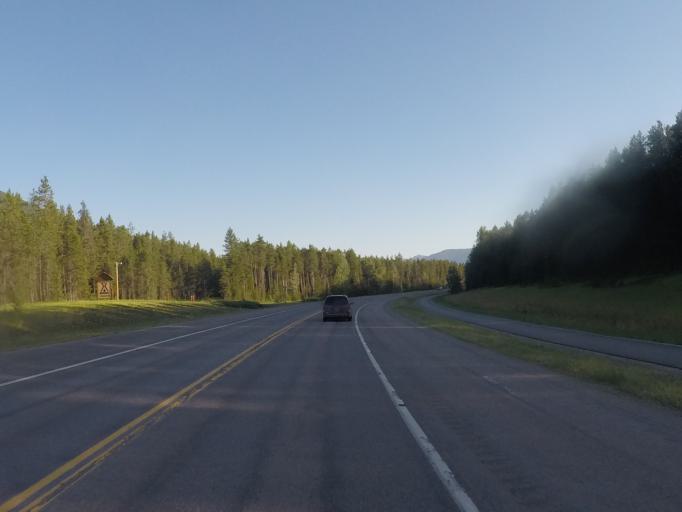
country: US
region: Montana
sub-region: Flathead County
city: Columbia Falls
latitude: 48.4678
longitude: -113.9967
